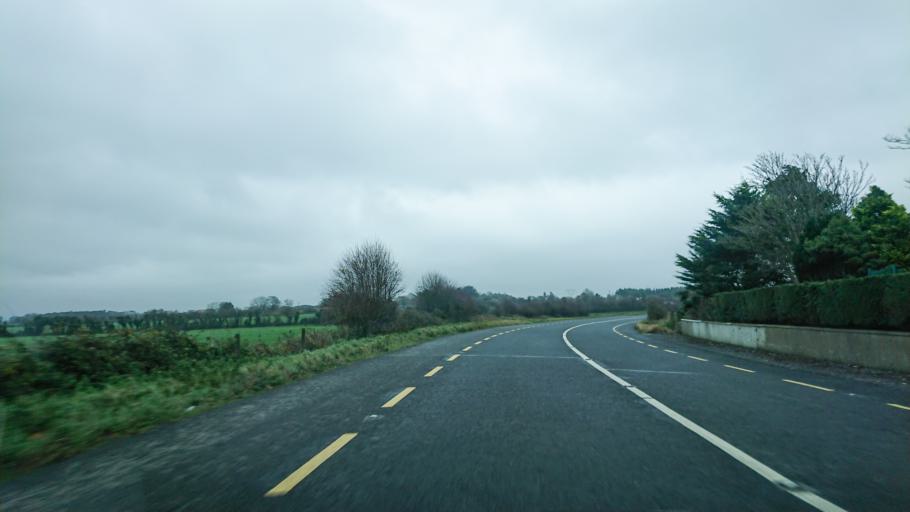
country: IE
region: Leinster
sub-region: Kilkenny
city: Mooncoin
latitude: 52.2826
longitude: -7.1967
